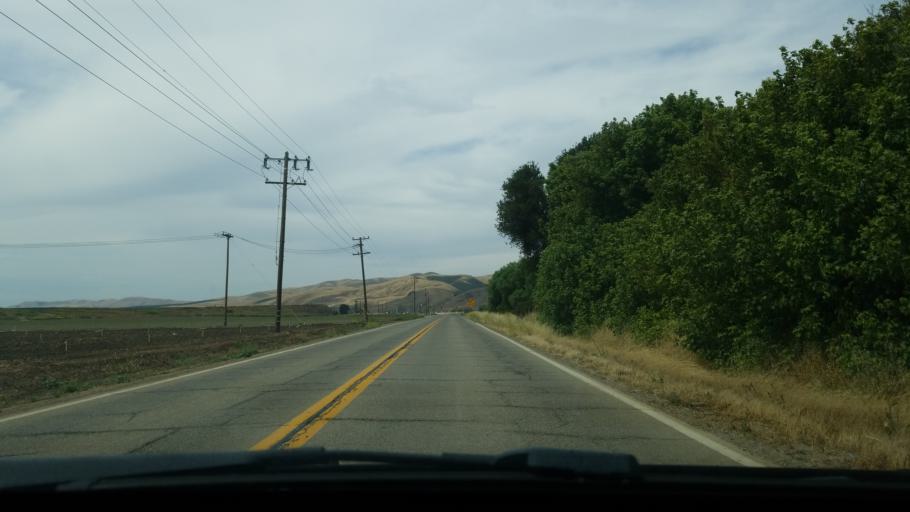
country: US
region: California
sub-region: Santa Barbara County
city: Orcutt
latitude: 34.8929
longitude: -120.3150
